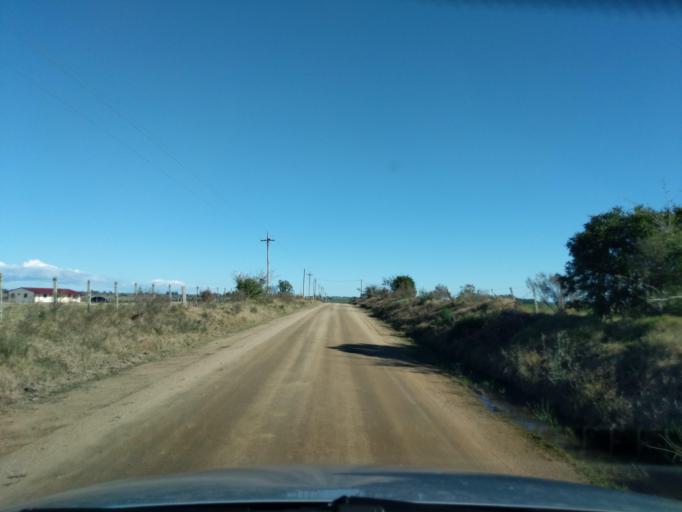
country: UY
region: Florida
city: Florida
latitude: -34.0819
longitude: -56.2527
